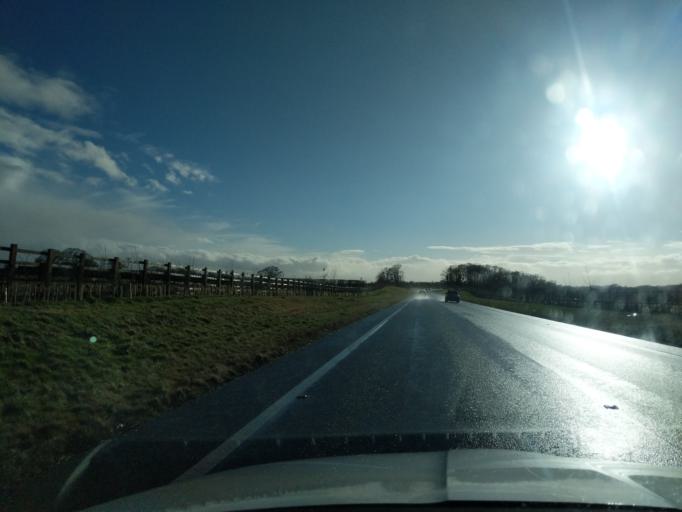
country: GB
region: England
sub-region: North Yorkshire
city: Bedale
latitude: 54.3035
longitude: -1.5843
